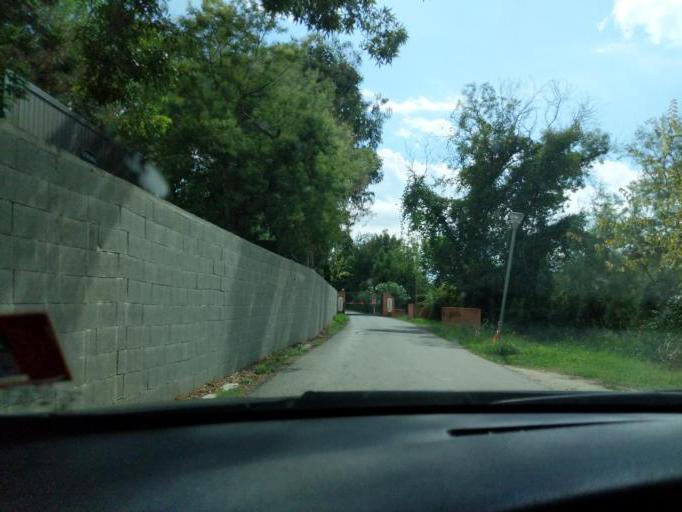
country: FR
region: Corsica
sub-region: Departement de la Haute-Corse
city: Ghisonaccia
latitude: 41.9970
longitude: 9.4412
